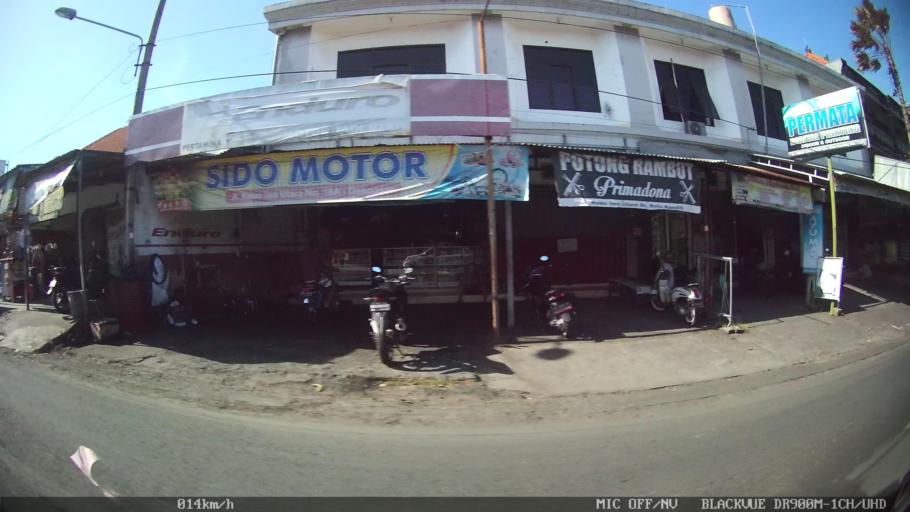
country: ID
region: Bali
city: Banjar Karangsuling
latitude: -8.6193
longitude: 115.1841
